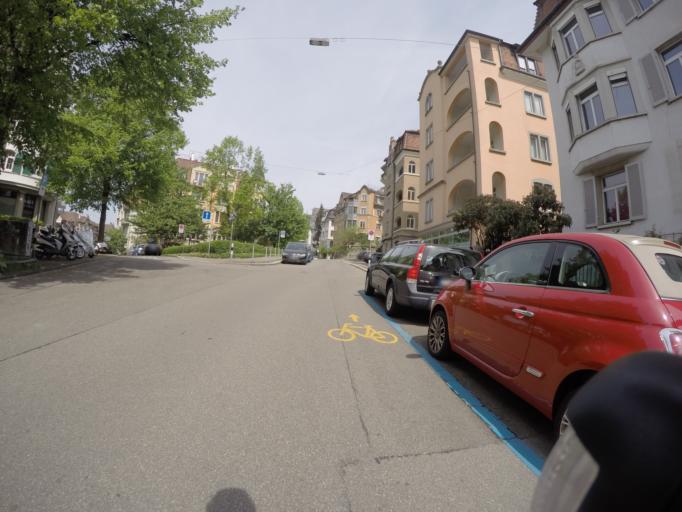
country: CH
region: Zurich
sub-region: Bezirk Zuerich
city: Zuerich (Kreis 6) / Oberstrass
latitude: 47.3830
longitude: 8.5453
